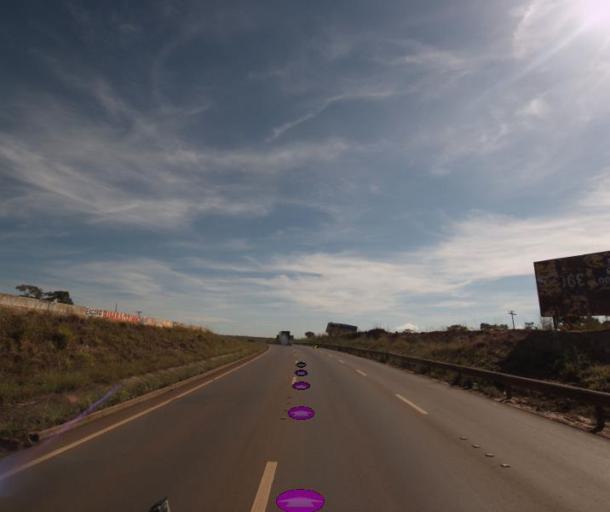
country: BR
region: Federal District
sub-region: Brasilia
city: Brasilia
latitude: -15.7701
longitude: -48.2300
